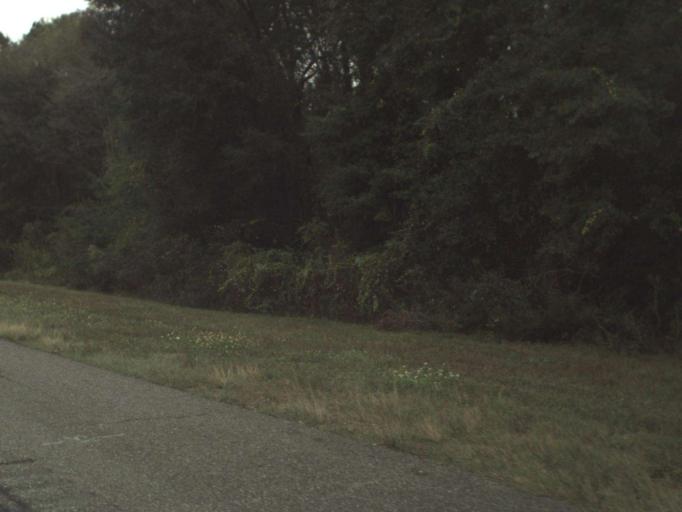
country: US
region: Florida
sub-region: Gadsden County
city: Midway
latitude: 30.4866
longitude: -84.4149
